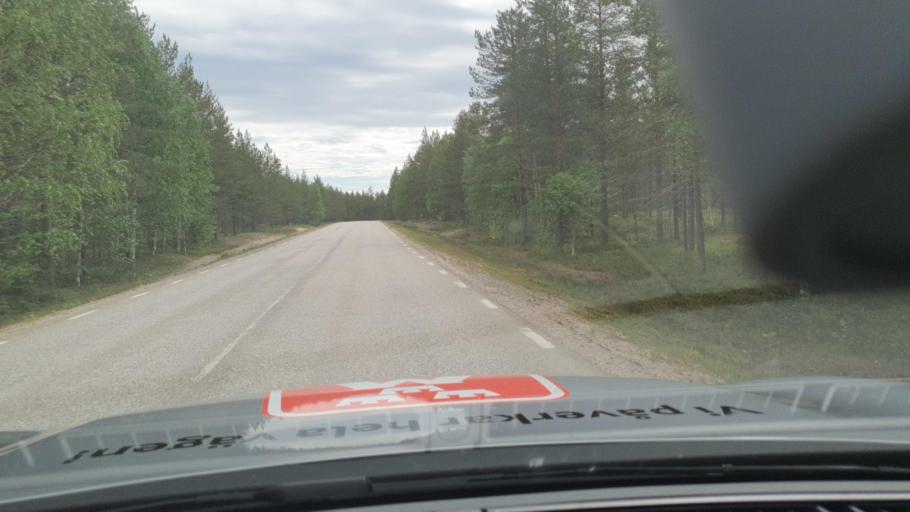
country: SE
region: Norrbotten
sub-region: Kalix Kommun
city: Kalix
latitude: 65.9087
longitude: 23.1740
